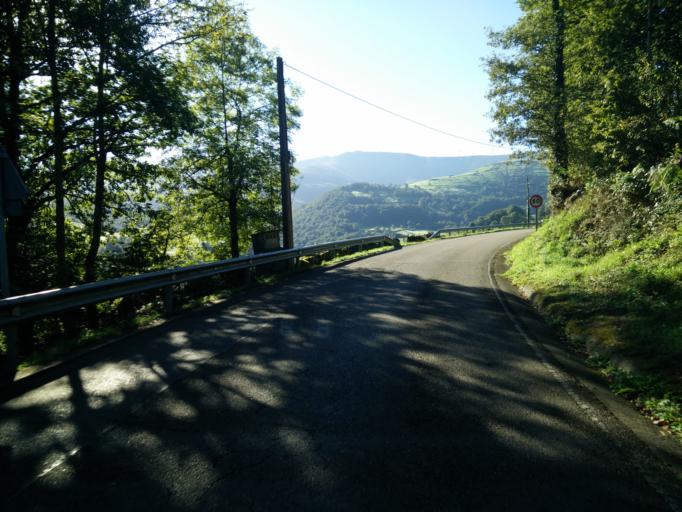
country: ES
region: Cantabria
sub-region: Provincia de Cantabria
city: San Pedro del Romeral
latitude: 43.1174
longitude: -3.8072
